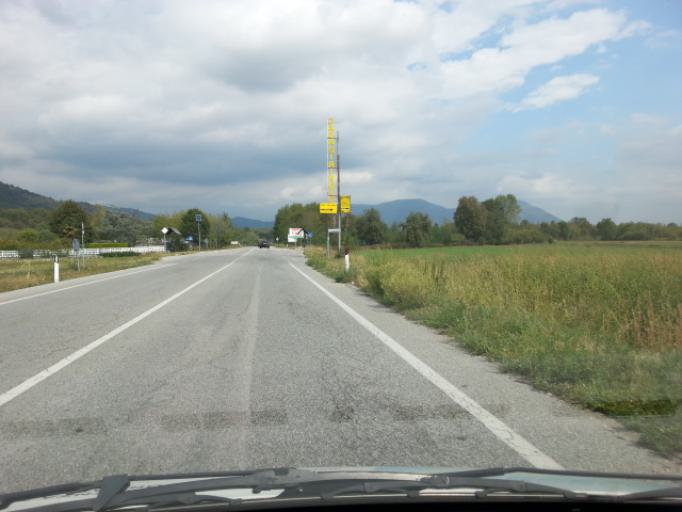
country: IT
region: Piedmont
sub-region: Provincia di Torino
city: Frossasco
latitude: 44.9344
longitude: 7.3713
